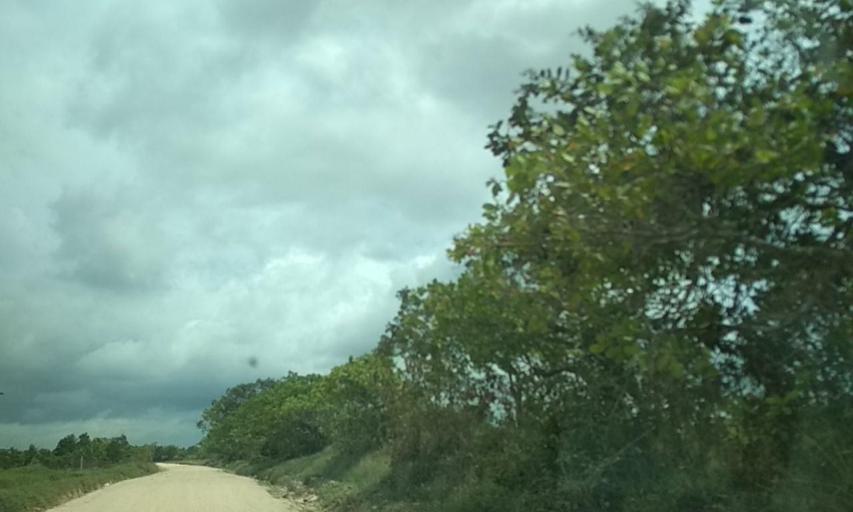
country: MX
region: Veracruz
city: Las Choapas
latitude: 17.9042
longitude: -94.1250
